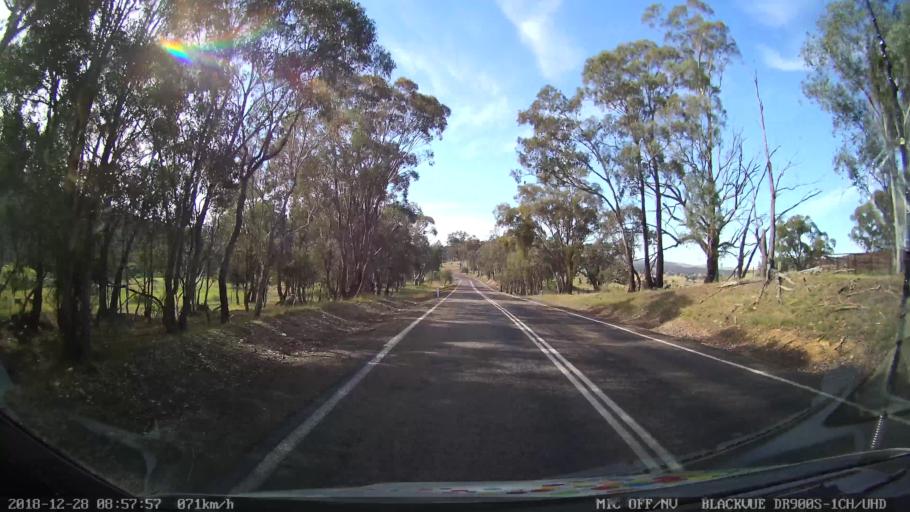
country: AU
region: New South Wales
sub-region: Upper Lachlan Shire
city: Crookwell
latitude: -34.1228
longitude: 149.3321
